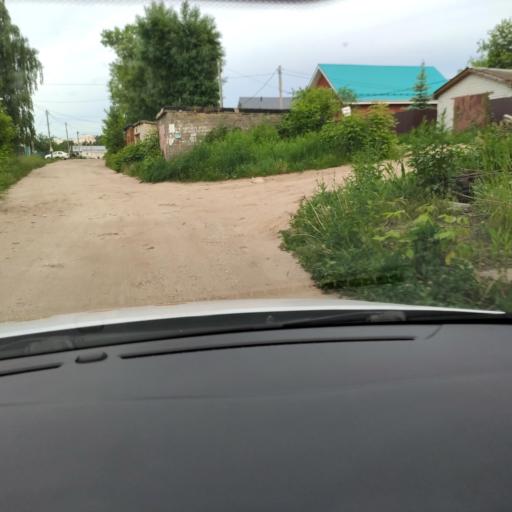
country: RU
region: Tatarstan
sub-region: Gorod Kazan'
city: Kazan
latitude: 55.8594
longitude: 49.0647
